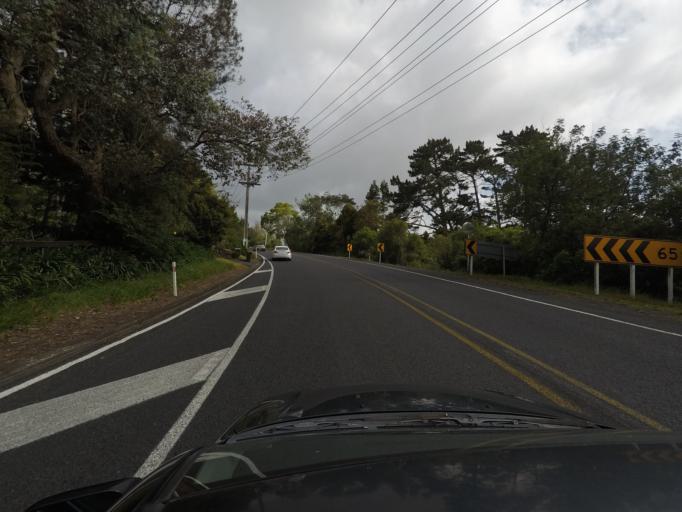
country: NZ
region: Auckland
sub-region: Auckland
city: Pakuranga
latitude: -36.9272
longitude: 174.9354
